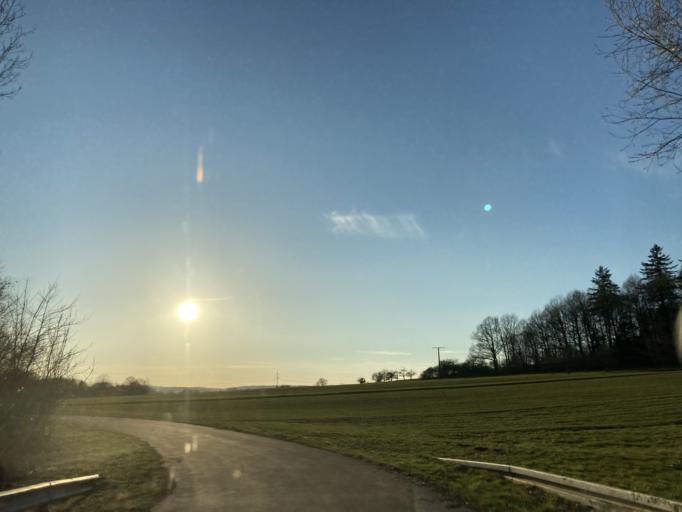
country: DE
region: Baden-Wuerttemberg
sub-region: Tuebingen Region
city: Nehren
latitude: 48.4086
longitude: 9.0877
